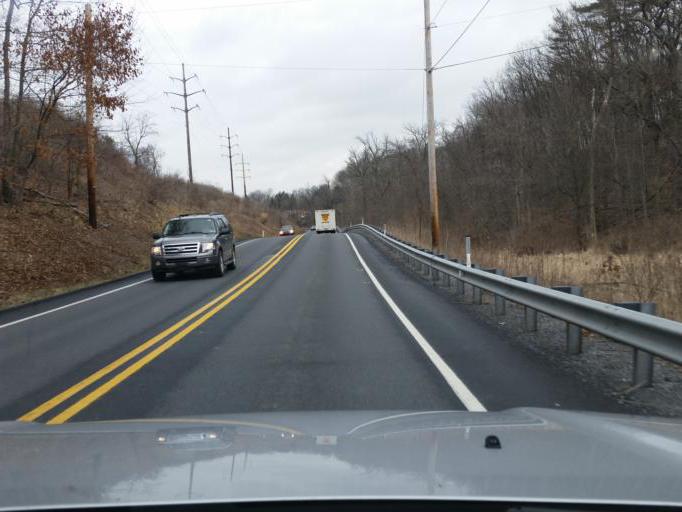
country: US
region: Pennsylvania
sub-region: Dauphin County
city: Rutherford
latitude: 40.3010
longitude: -76.7664
